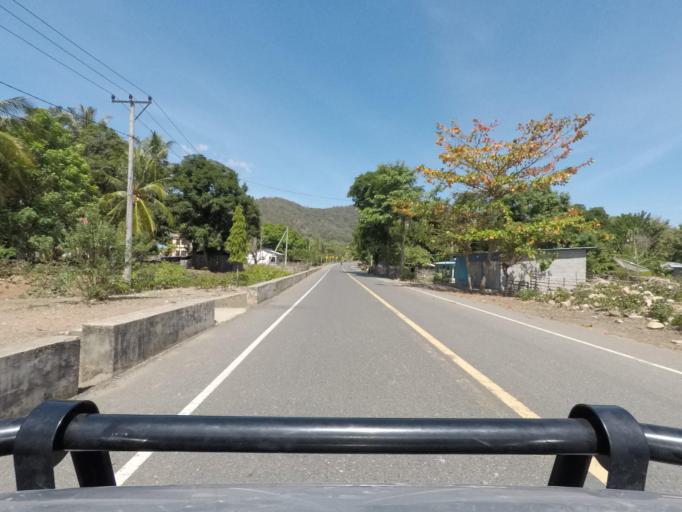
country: TL
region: Liquica
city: Maubara
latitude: -8.7935
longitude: 125.1016
